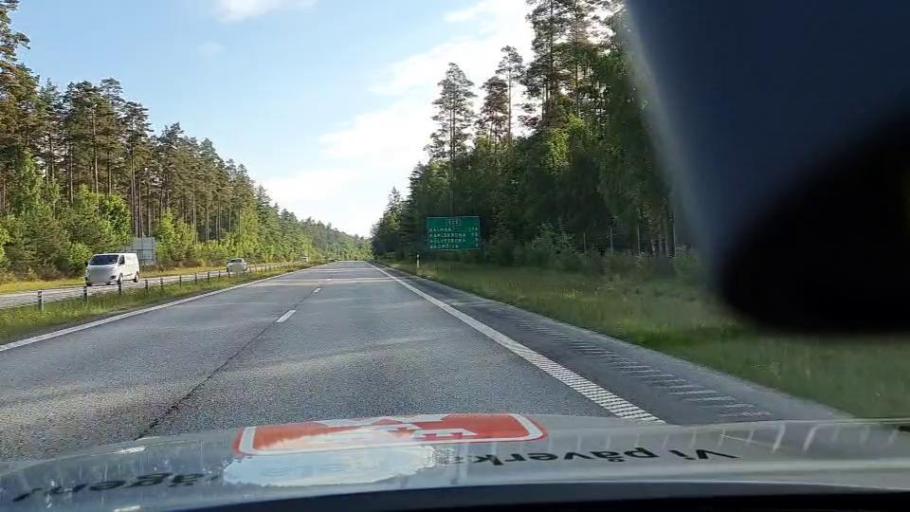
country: SE
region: Skane
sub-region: Bromolla Kommun
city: Bromoella
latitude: 56.0530
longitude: 14.4439
